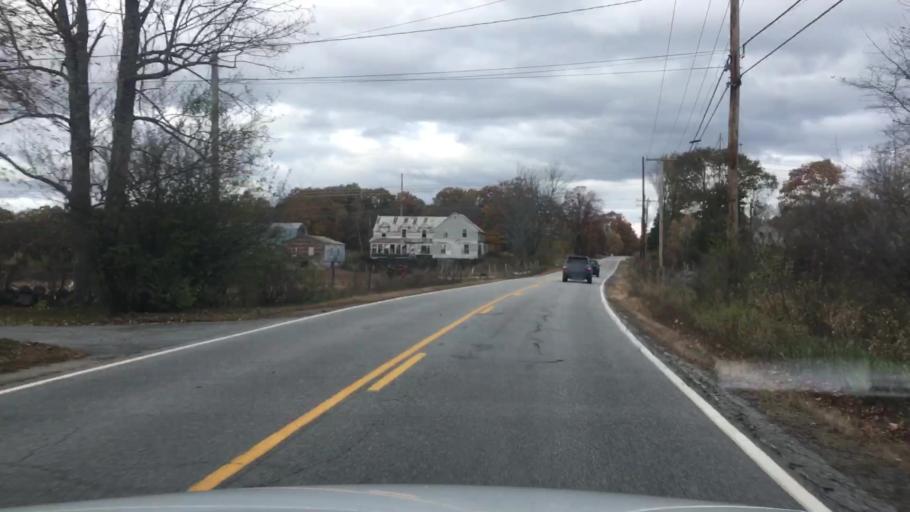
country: US
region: Maine
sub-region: Androscoggin County
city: Sabattus
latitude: 44.1762
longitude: -70.0697
